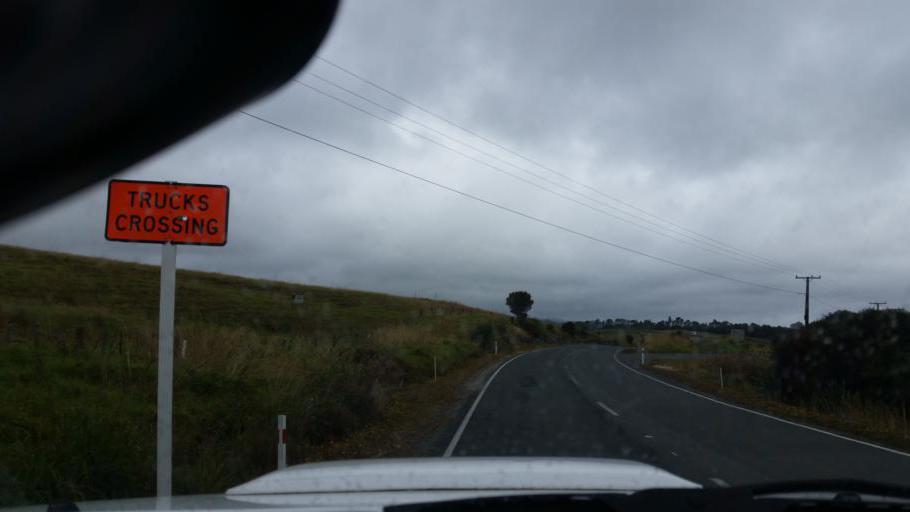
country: NZ
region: Auckland
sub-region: Auckland
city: Wellsford
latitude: -36.1432
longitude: 174.4986
